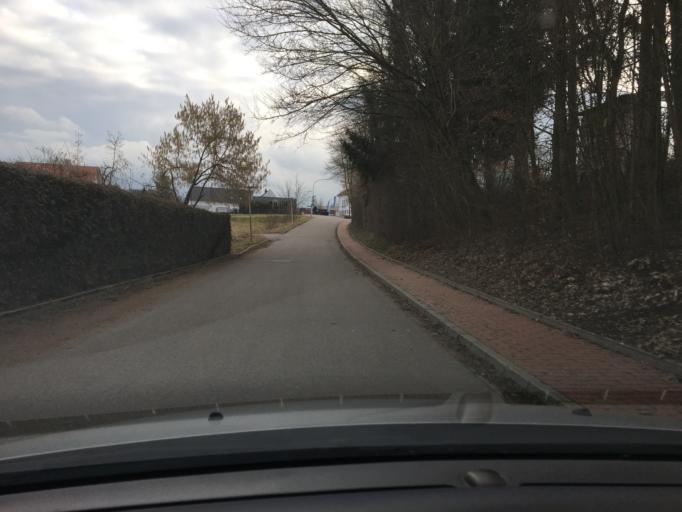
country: DE
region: Bavaria
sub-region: Lower Bavaria
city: Tiefenbach
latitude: 48.4873
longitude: 12.0922
